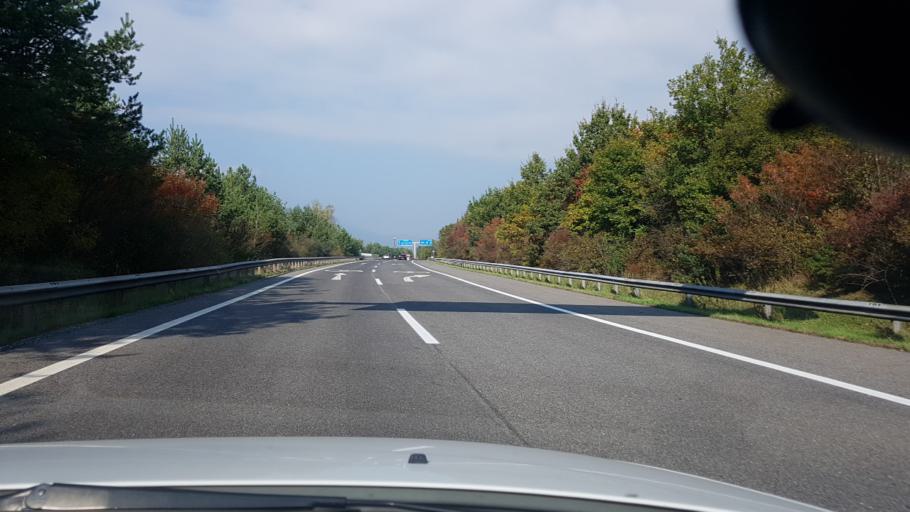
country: AT
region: Carinthia
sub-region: Politischer Bezirk Villach Land
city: Wernberg
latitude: 46.6166
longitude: 13.9062
